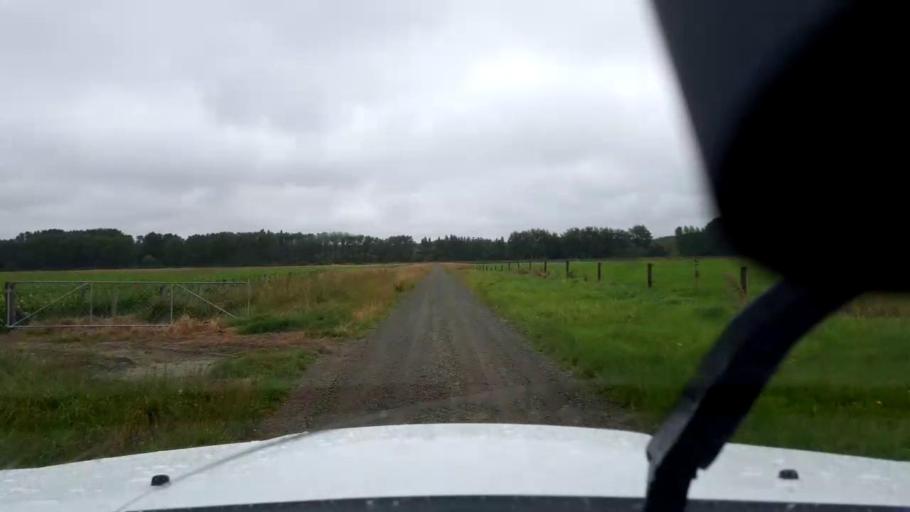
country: NZ
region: Canterbury
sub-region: Timaru District
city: Pleasant Point
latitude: -44.2555
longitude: 171.1996
